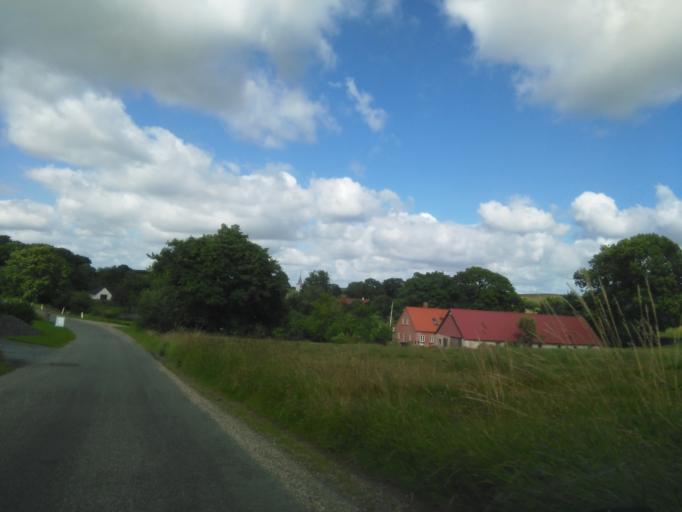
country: DK
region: Central Jutland
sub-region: Syddjurs Kommune
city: Ronde
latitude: 56.2292
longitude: 10.5213
